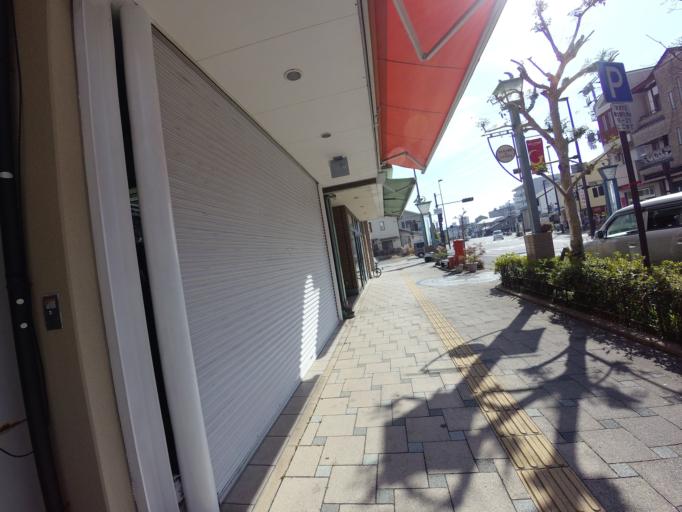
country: JP
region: Wakayama
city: Tanabe
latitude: 33.7328
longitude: 135.3787
